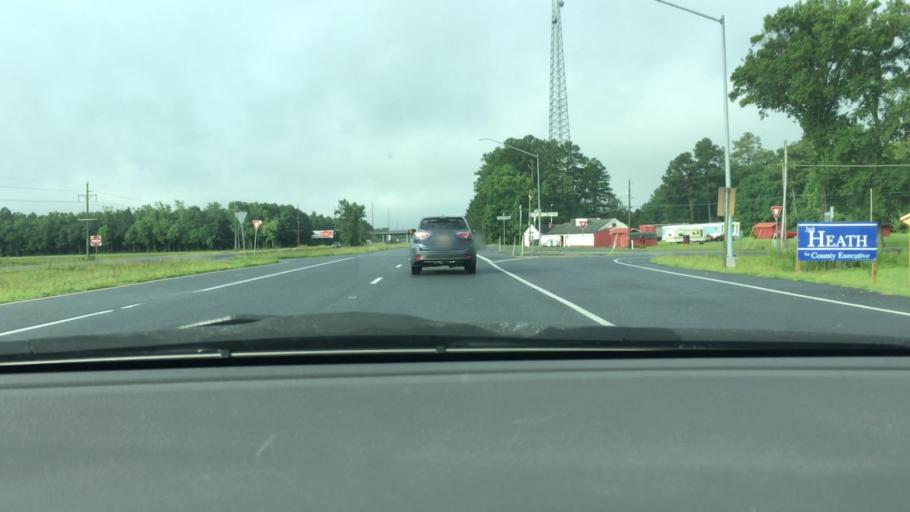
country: US
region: Maryland
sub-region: Wicomico County
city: Fruitland
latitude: 38.3076
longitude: -75.6305
